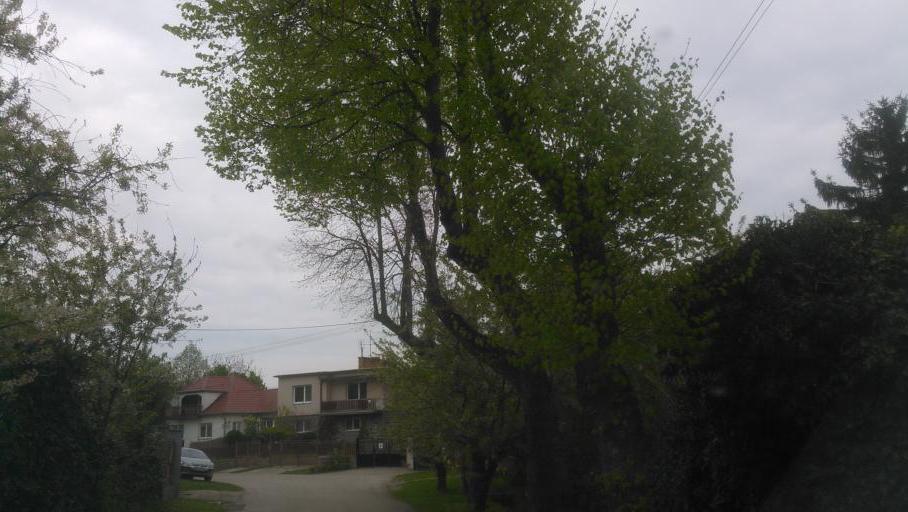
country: SK
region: Bratislavsky
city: Senec
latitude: 48.1460
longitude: 17.3398
